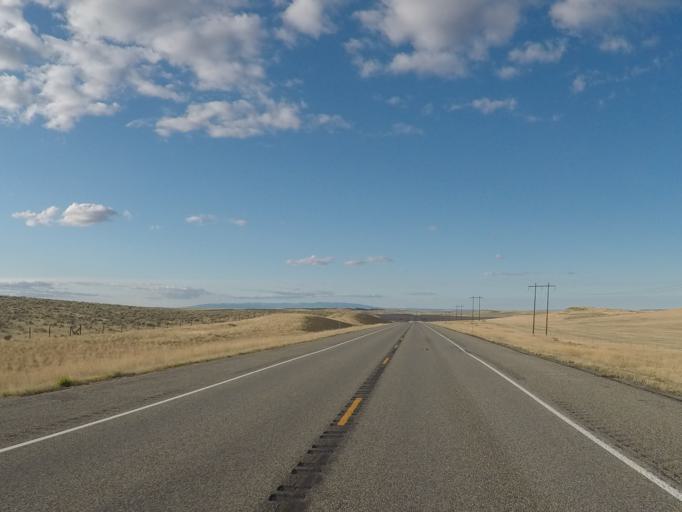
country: US
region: Montana
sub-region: Golden Valley County
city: Ryegate
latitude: 46.1829
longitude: -108.9112
